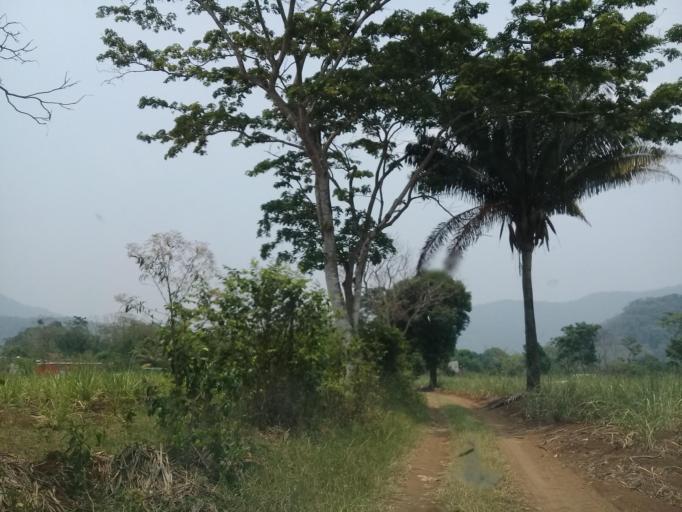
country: MX
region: Veracruz
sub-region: Tezonapa
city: Laguna Chica (Pueblo Nuevo)
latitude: 18.5391
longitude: -96.7377
